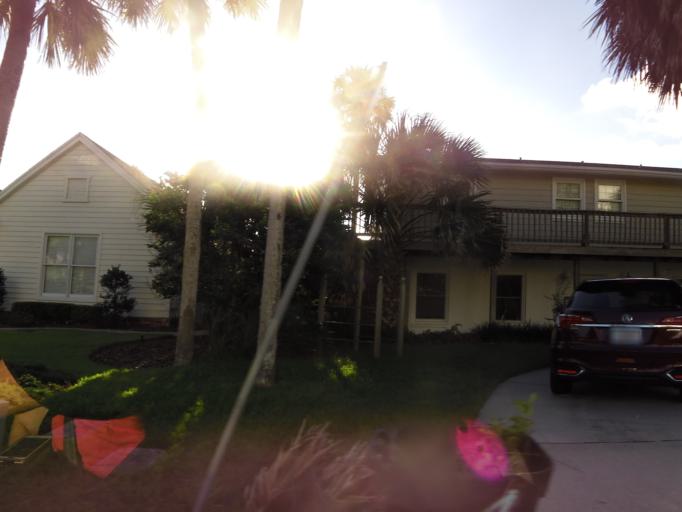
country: US
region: Florida
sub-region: Saint Johns County
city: Ponte Vedra Beach
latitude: 30.2570
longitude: -81.3827
